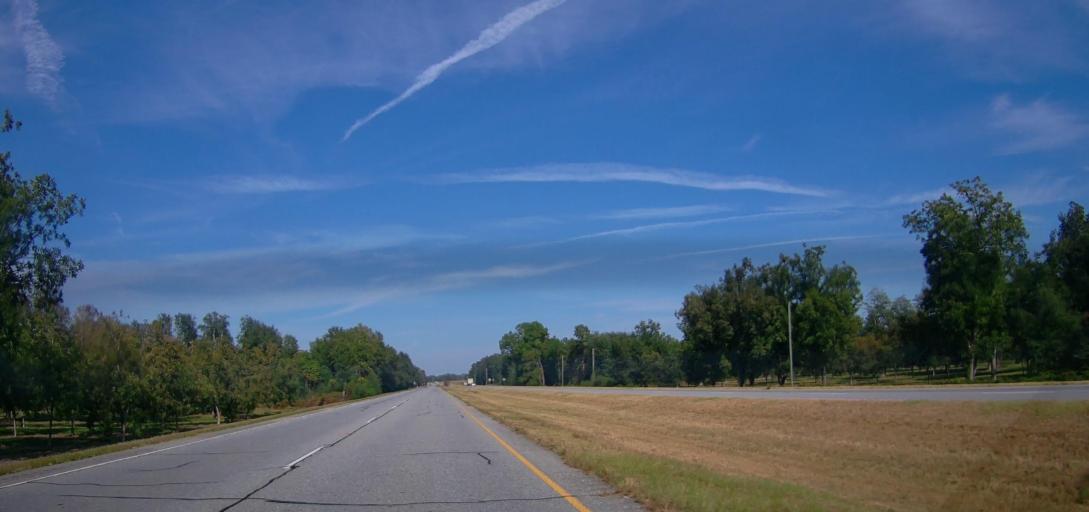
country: US
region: Georgia
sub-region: Dougherty County
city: Putney
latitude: 31.3510
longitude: -84.1625
